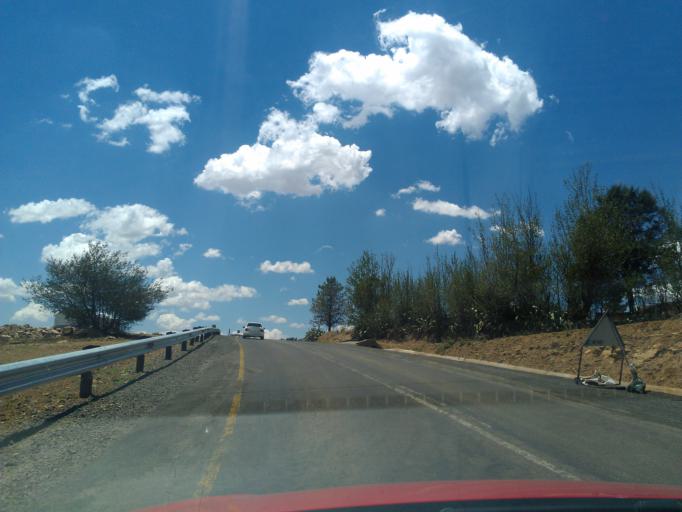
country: LS
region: Leribe
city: Maputsoe
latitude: -29.0921
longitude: 27.9588
